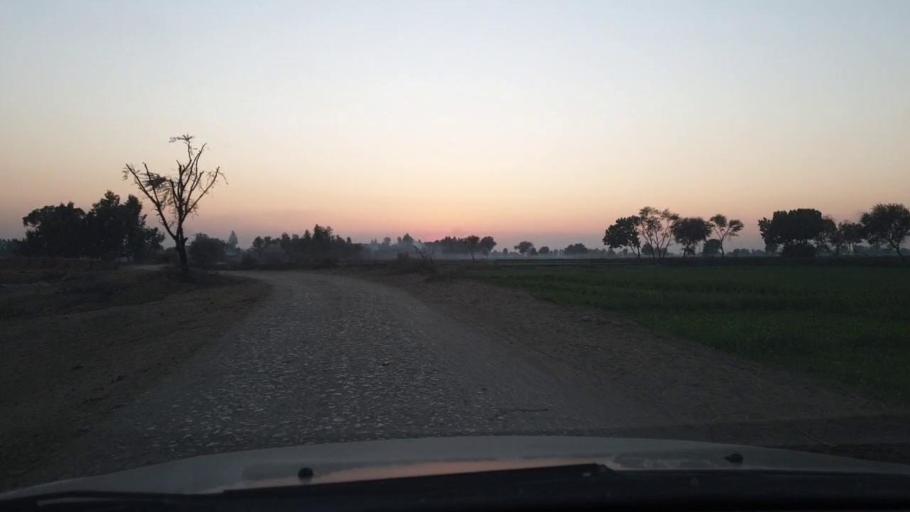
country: PK
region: Sindh
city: Mirpur Mathelo
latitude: 28.0254
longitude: 69.5186
